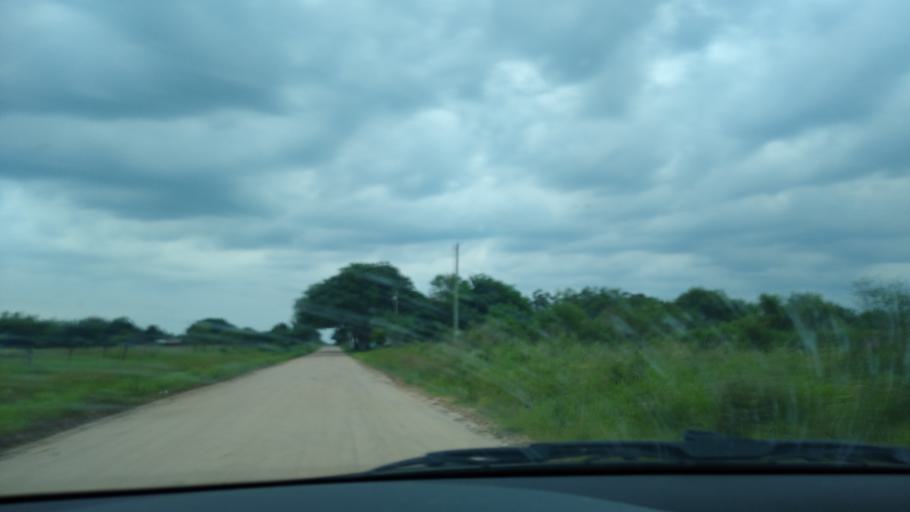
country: AR
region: Chaco
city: Puerto Vilelas
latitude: -27.5117
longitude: -58.9684
